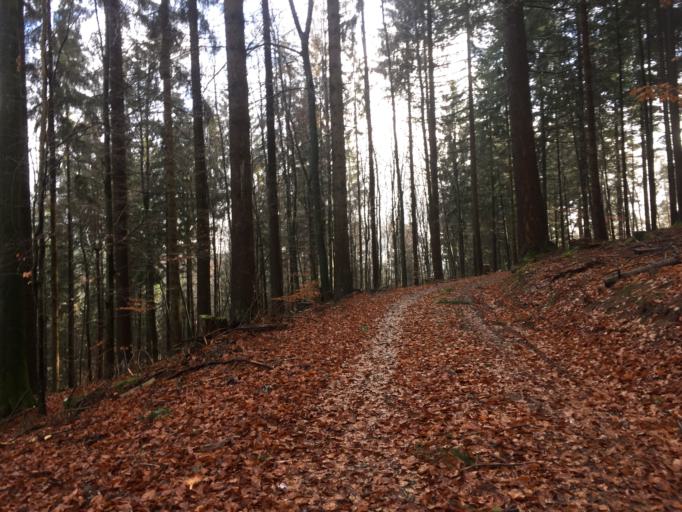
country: DE
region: Hesse
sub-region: Regierungsbezirk Darmstadt
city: Wald-Michelbach
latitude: 49.5586
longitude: 8.8937
